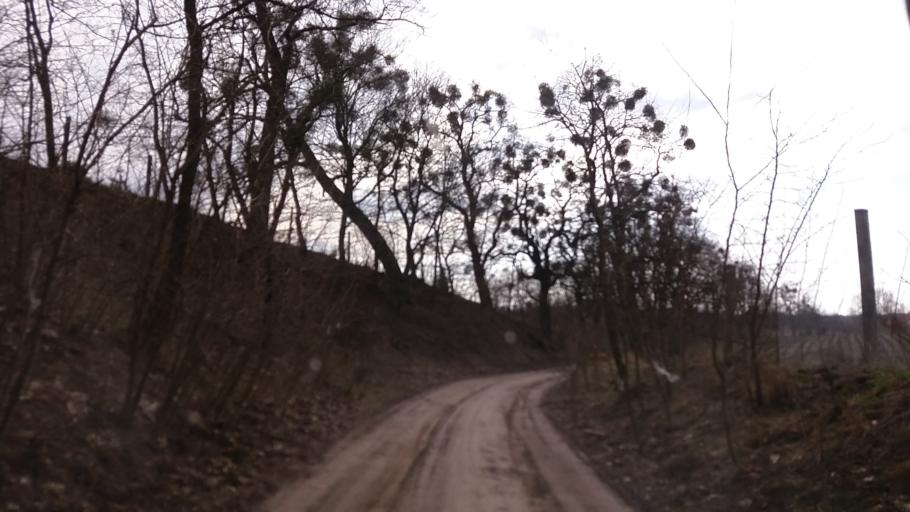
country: PL
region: West Pomeranian Voivodeship
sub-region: Powiat choszczenski
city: Bierzwnik
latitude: 53.1183
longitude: 15.6294
